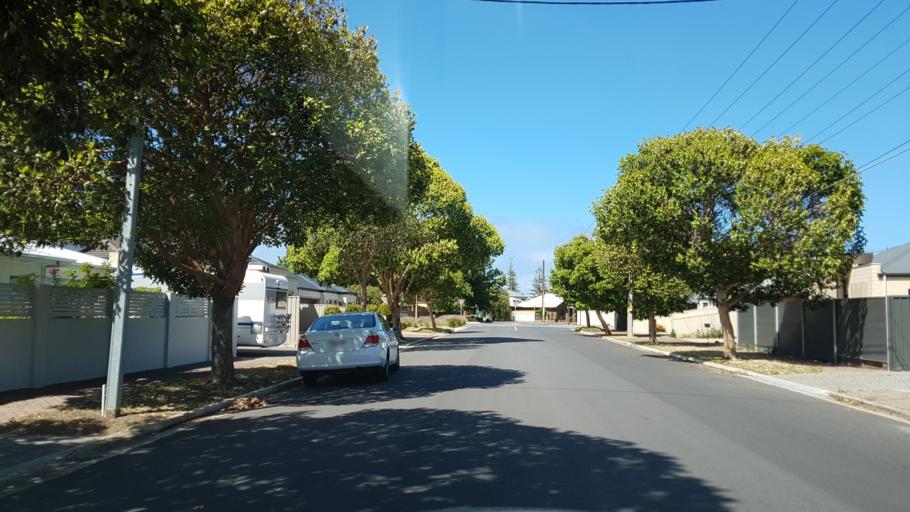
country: AU
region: South Australia
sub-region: Holdfast Bay
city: Glenelg East
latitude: -34.9682
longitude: 138.5197
